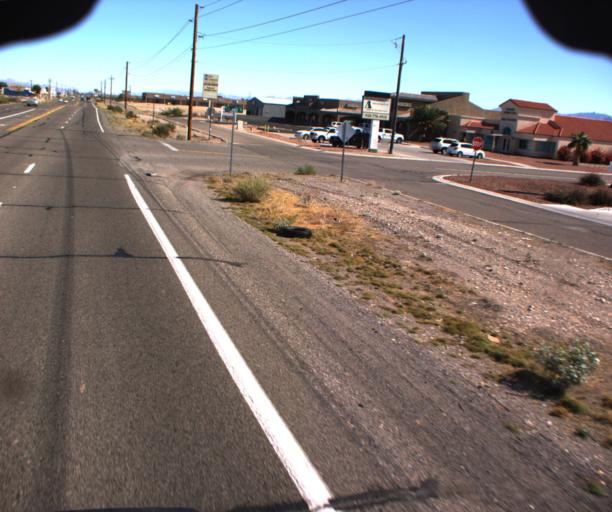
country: US
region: Arizona
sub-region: Mohave County
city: Mohave Valley
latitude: 34.9864
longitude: -114.5979
